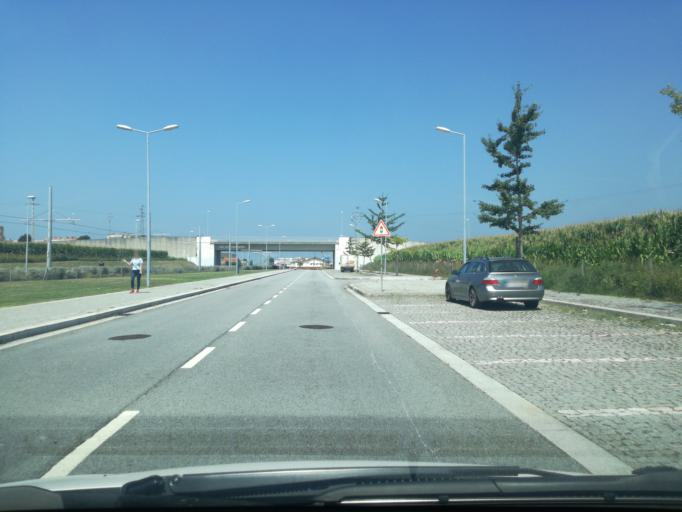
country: PT
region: Porto
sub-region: Matosinhos
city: Santa Cruz do Bispo
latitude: 41.2410
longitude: -8.6589
